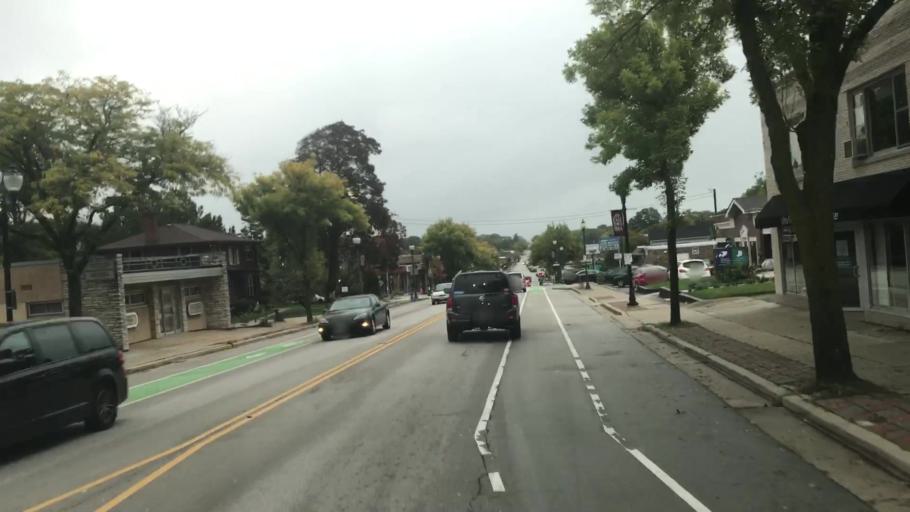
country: US
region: Wisconsin
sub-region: Milwaukee County
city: Wauwatosa
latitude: 43.0607
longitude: -88.0019
